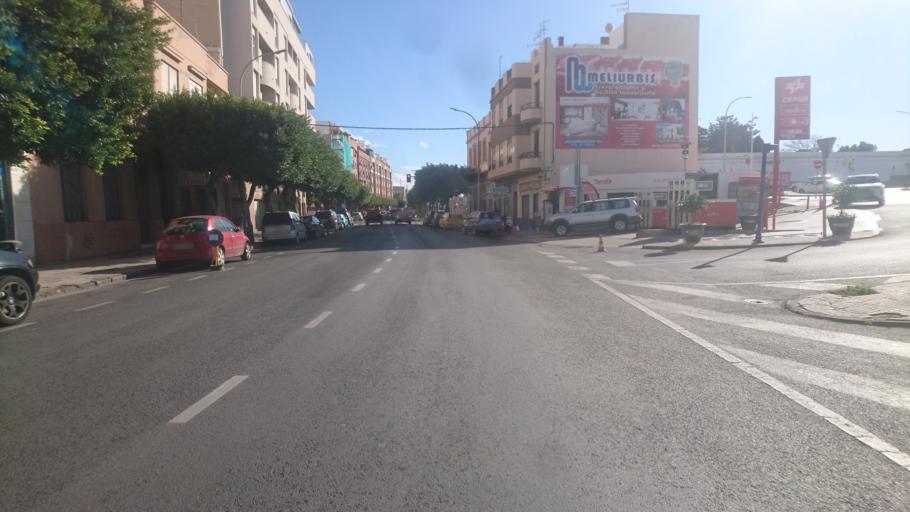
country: ES
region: Melilla
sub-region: Melilla
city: Melilla
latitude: 35.2817
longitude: -2.9413
